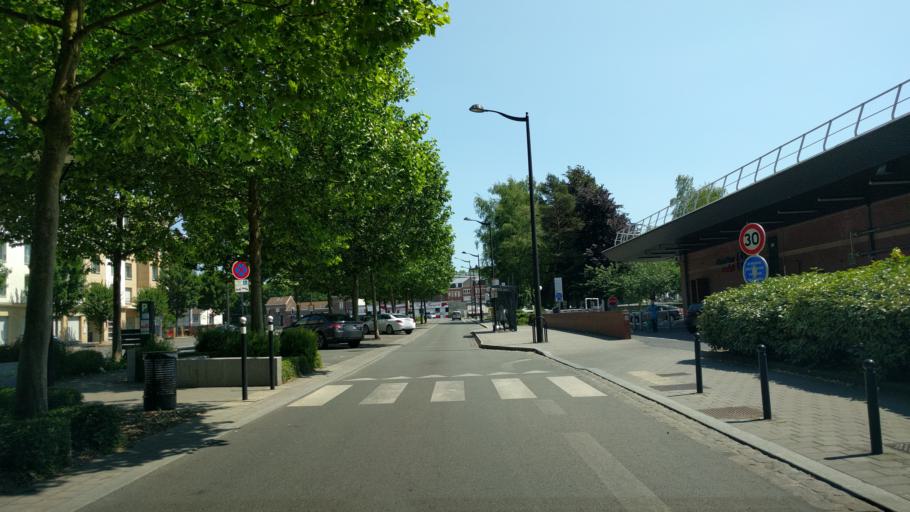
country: FR
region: Nord-Pas-de-Calais
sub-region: Departement du Nord
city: Valenciennes
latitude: 50.3640
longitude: 3.5270
